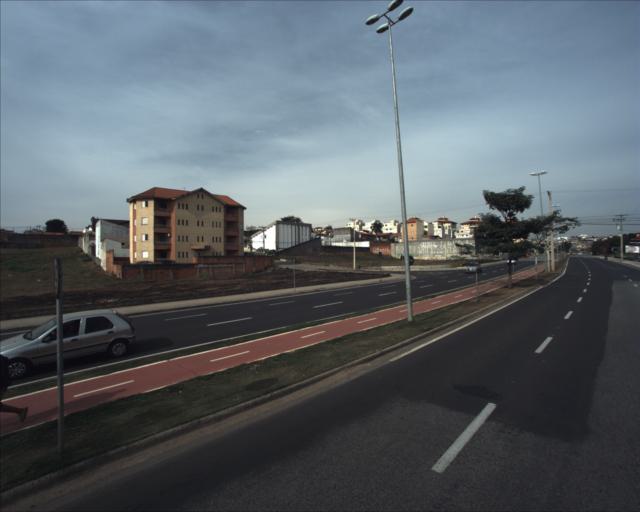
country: BR
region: Sao Paulo
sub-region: Sorocaba
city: Sorocaba
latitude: -23.4783
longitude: -47.4557
